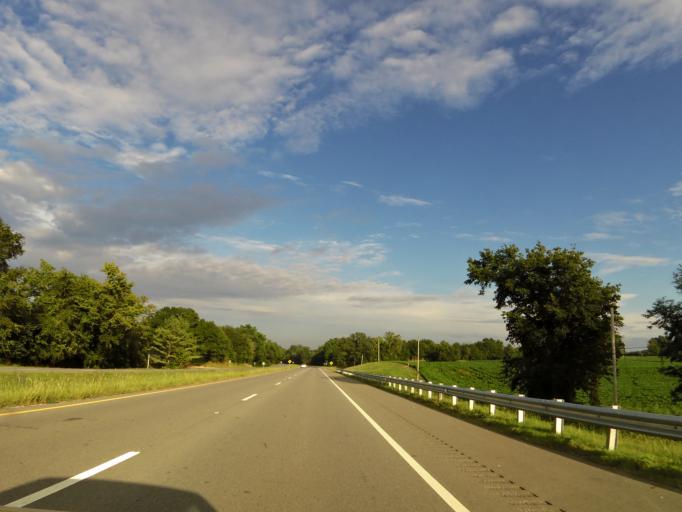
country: US
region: Alabama
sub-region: Lauderdale County
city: Rogersville
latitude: 34.8351
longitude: -87.3415
